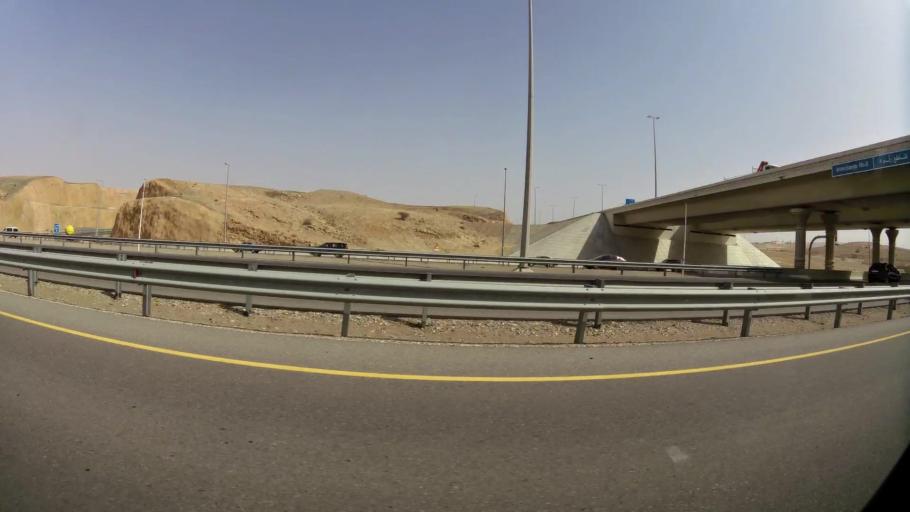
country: OM
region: Muhafazat Masqat
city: Bawshar
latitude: 23.5613
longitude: 58.3390
